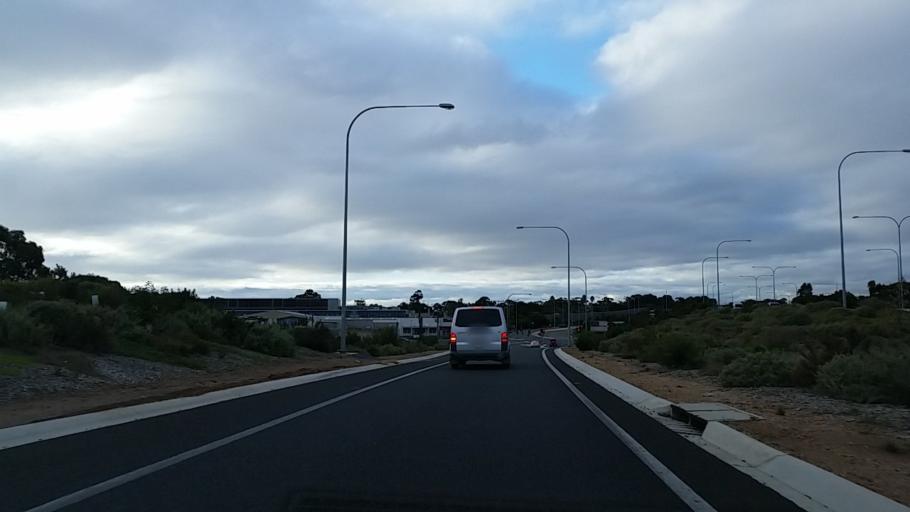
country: AU
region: South Australia
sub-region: Onkaparinga
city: Reynella
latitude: -35.1080
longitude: 138.5089
